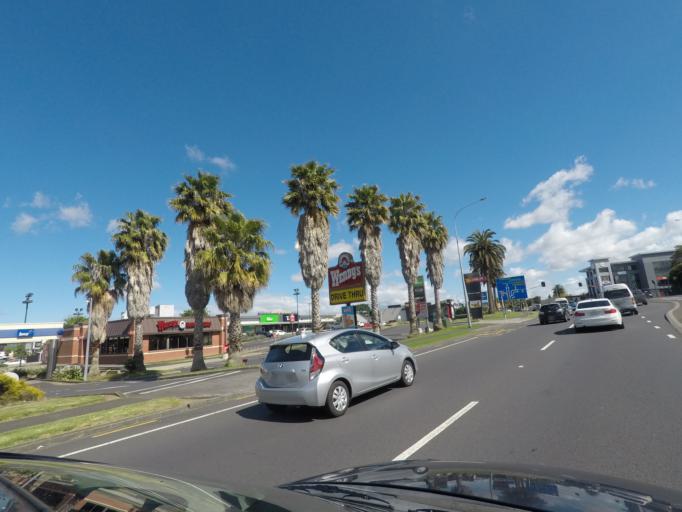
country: NZ
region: Auckland
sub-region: Auckland
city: Manukau City
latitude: -36.9890
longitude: 174.8829
